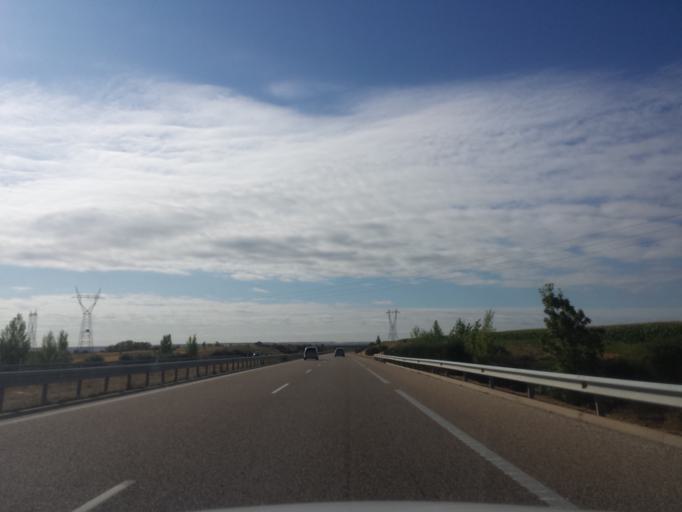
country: ES
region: Castille and Leon
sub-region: Provincia de Leon
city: Villamanan
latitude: 42.3112
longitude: -5.5992
